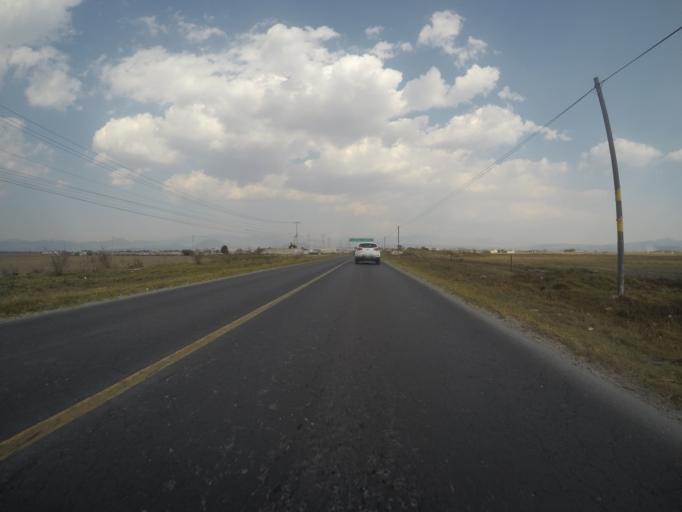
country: MX
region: Mexico
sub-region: Atizapan
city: Colonia la Libertad
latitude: 19.1912
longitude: -99.5318
